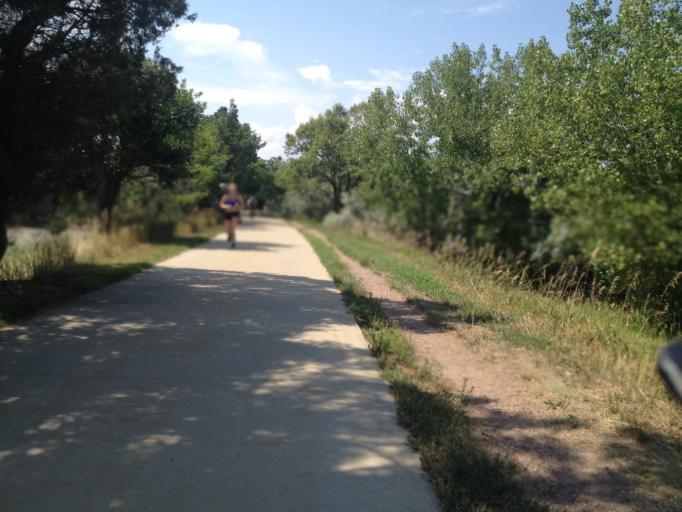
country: US
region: Colorado
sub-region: Boulder County
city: Boulder
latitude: 40.0254
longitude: -105.2173
